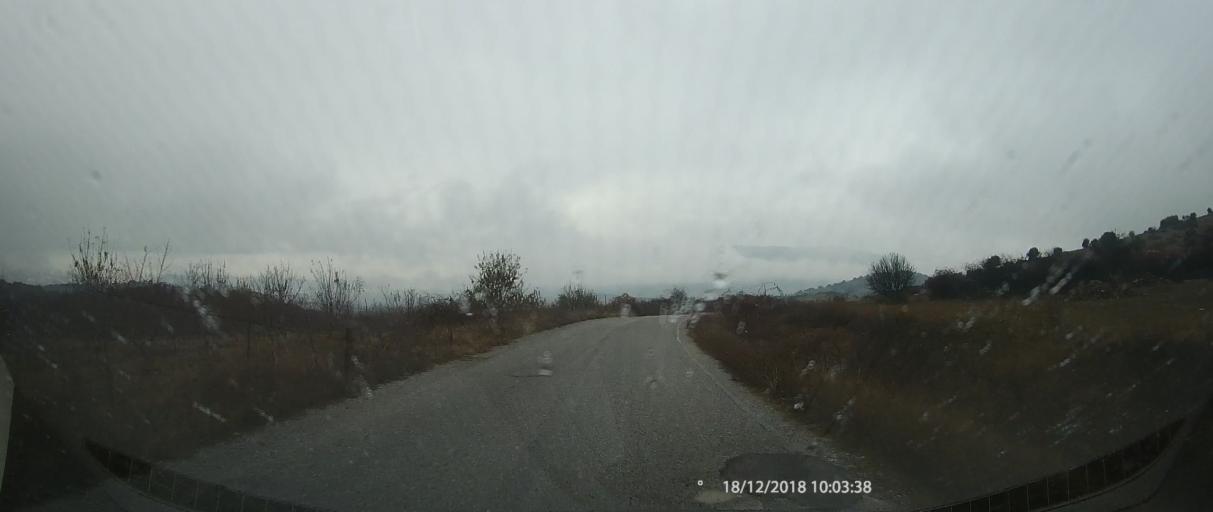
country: GR
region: Thessaly
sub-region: Nomos Larisis
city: Livadi
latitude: 40.0446
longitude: 22.2252
